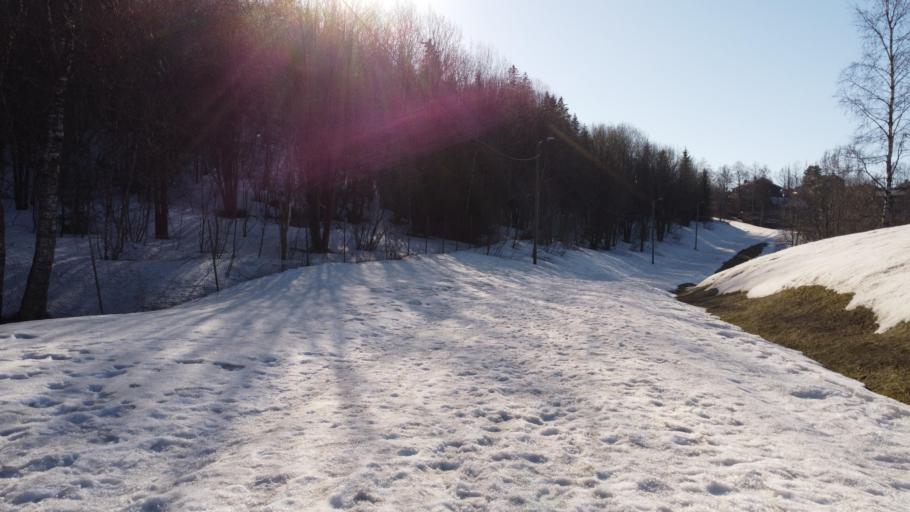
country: NO
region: Nordland
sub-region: Rana
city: Mo i Rana
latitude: 66.3147
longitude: 14.1713
